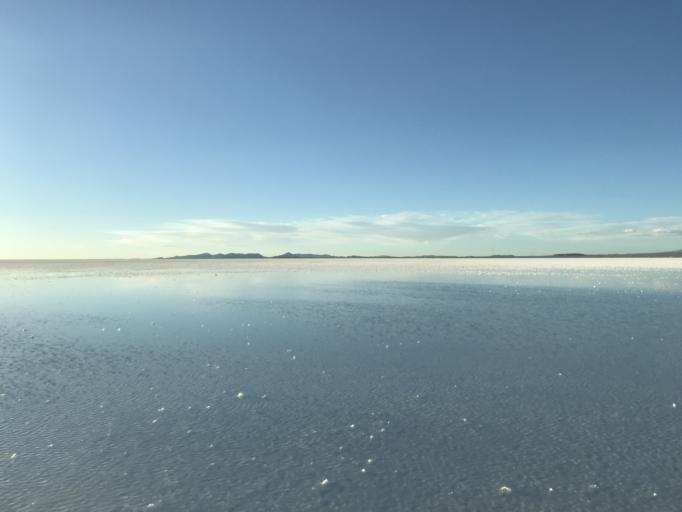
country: BO
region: Potosi
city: Colchani
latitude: -20.3861
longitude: -66.9838
